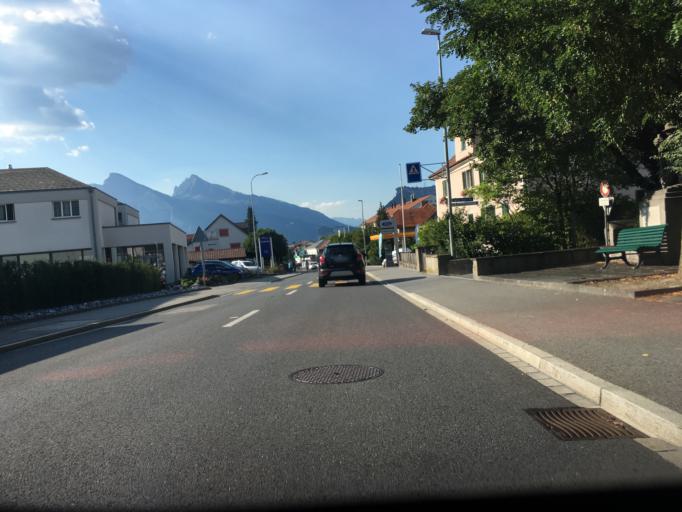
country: CH
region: Saint Gallen
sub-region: Wahlkreis Sarganserland
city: Bad Ragaz
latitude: 47.0052
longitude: 9.4999
